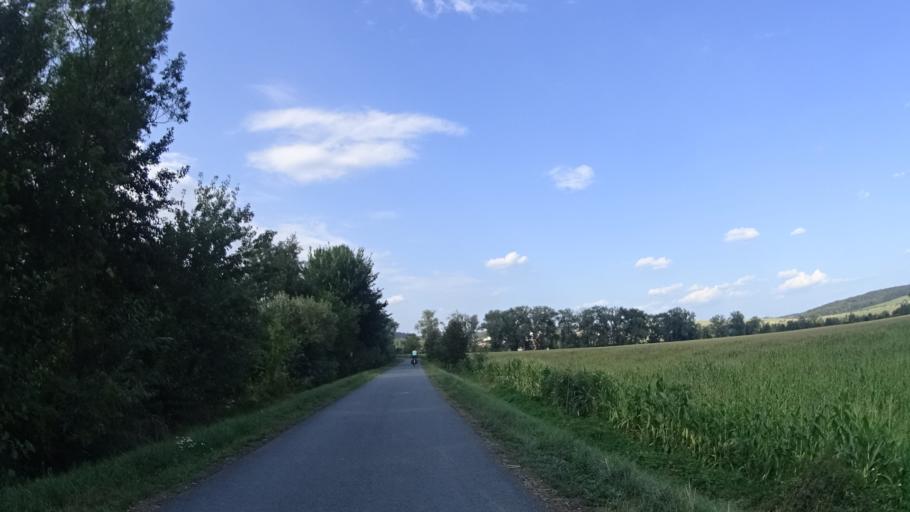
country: CZ
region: Zlin
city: Spytihnev
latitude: 49.1535
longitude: 17.5070
